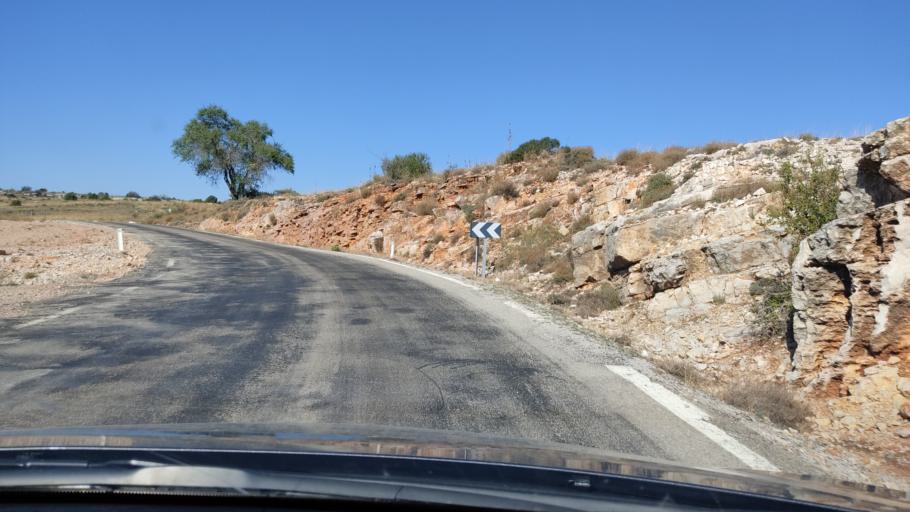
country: ES
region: Aragon
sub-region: Provincia de Teruel
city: Allueva
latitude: 41.0070
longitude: -1.0586
